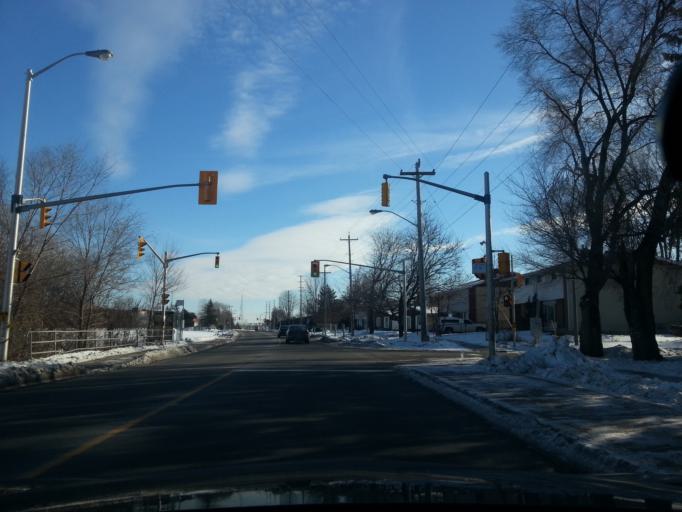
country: CA
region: Ontario
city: Ottawa
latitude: 45.3954
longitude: -75.6133
